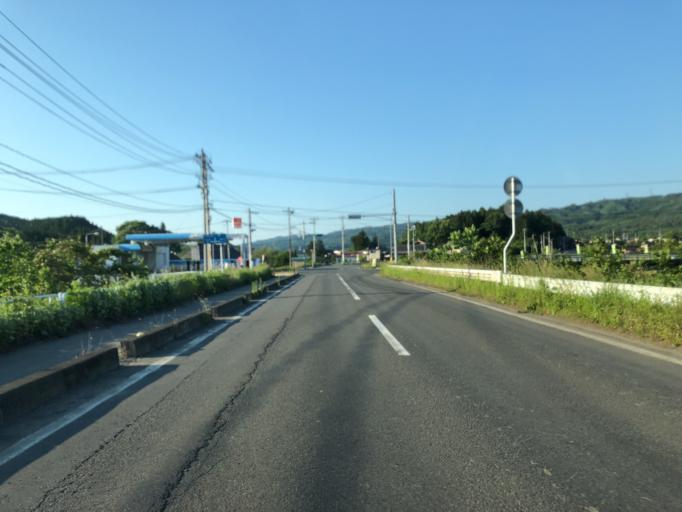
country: JP
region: Fukushima
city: Ishikawa
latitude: 36.9629
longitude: 140.4286
